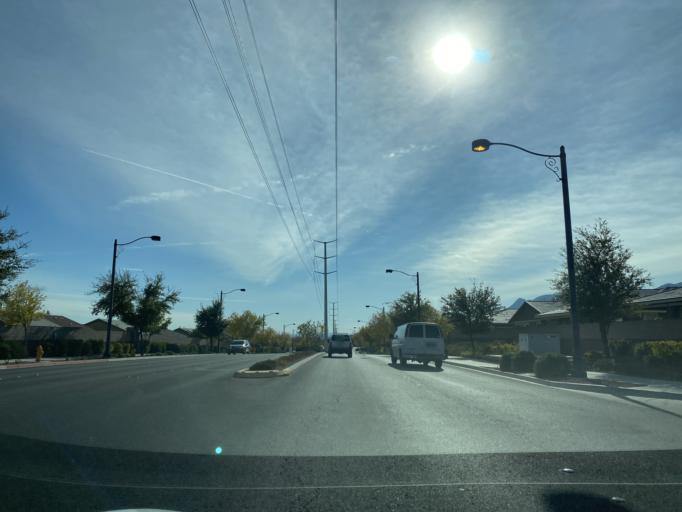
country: US
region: Nevada
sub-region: Clark County
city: Summerlin South
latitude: 36.2914
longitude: -115.3289
